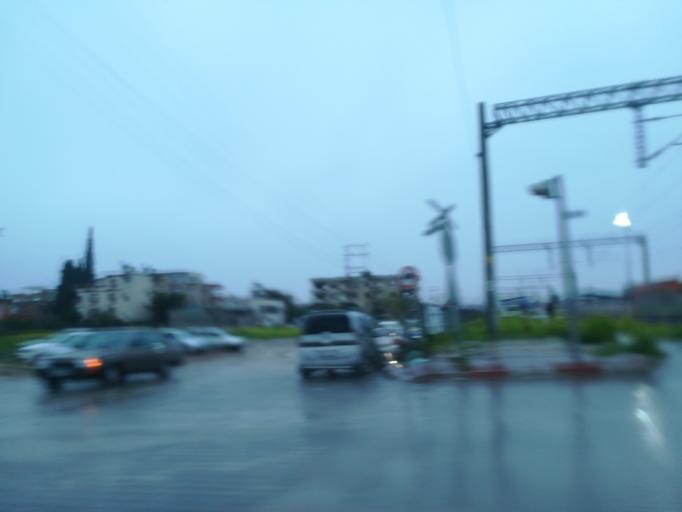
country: TR
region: Adana
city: Seyhan
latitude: 36.9964
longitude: 35.2879
